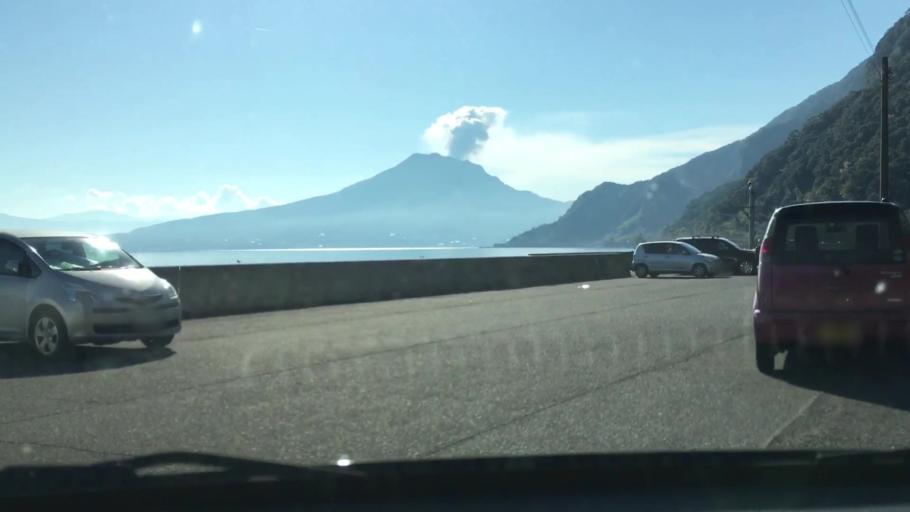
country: JP
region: Kagoshima
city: Kajiki
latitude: 31.6827
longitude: 130.6095
